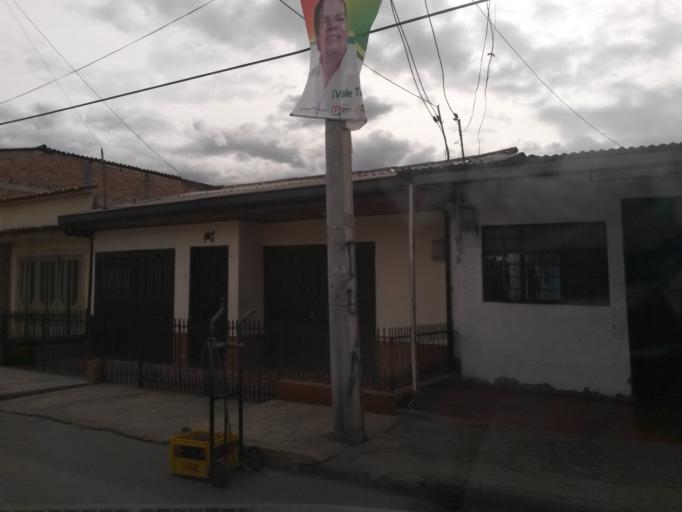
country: CO
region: Cauca
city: Popayan
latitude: 2.4511
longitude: -76.6243
